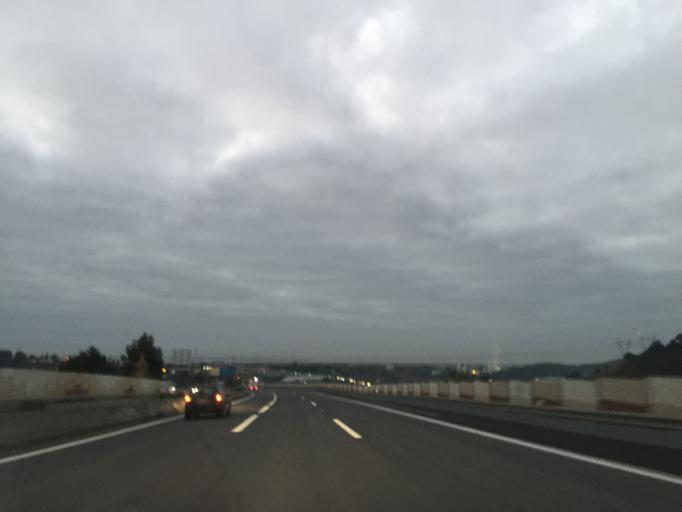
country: PT
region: Lisbon
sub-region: Vila Franca de Xira
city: Vialonga
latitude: 38.8985
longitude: -9.0552
